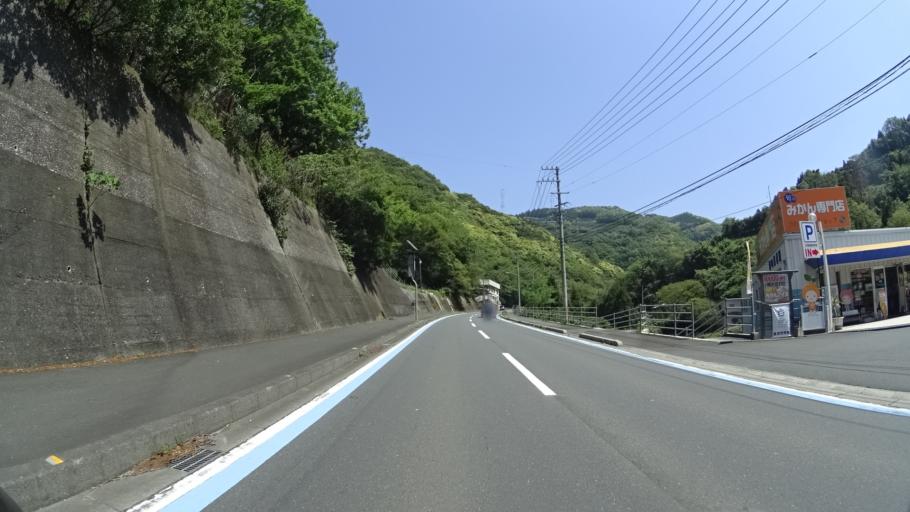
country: JP
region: Ehime
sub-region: Nishiuwa-gun
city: Ikata-cho
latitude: 33.4956
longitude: 132.3676
